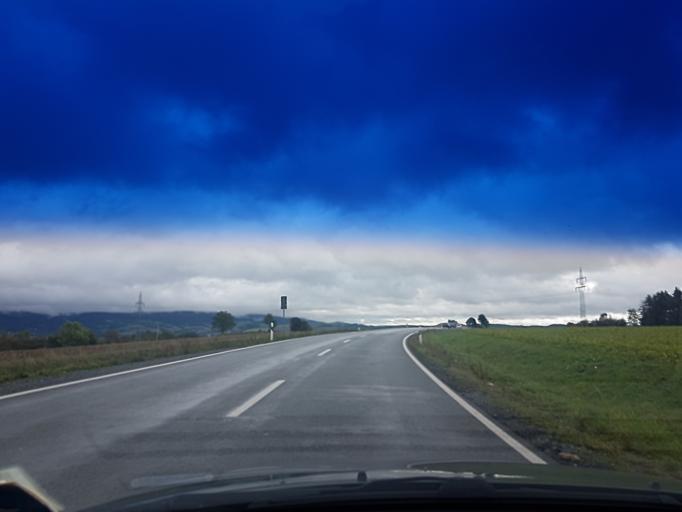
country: DE
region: Bavaria
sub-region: Upper Franconia
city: Bindlach
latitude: 50.0143
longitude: 11.6100
